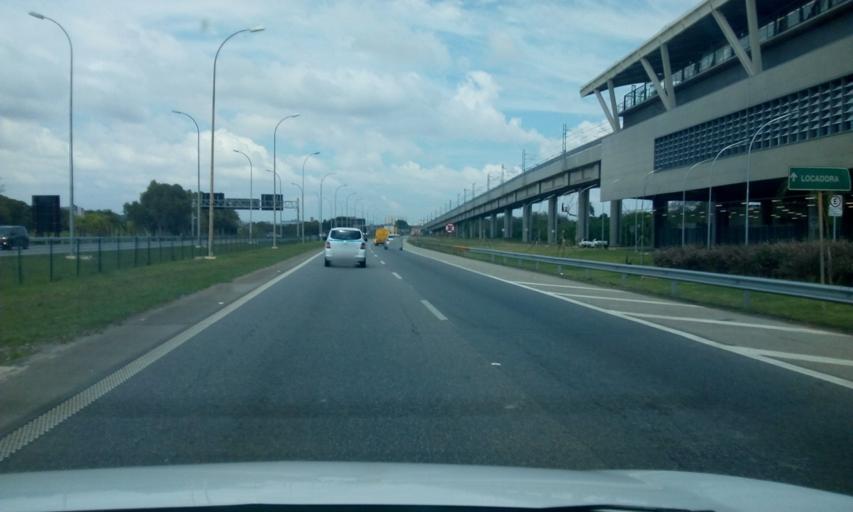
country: BR
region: Sao Paulo
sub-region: Guarulhos
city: Guarulhos
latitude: -23.4333
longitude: -46.4937
